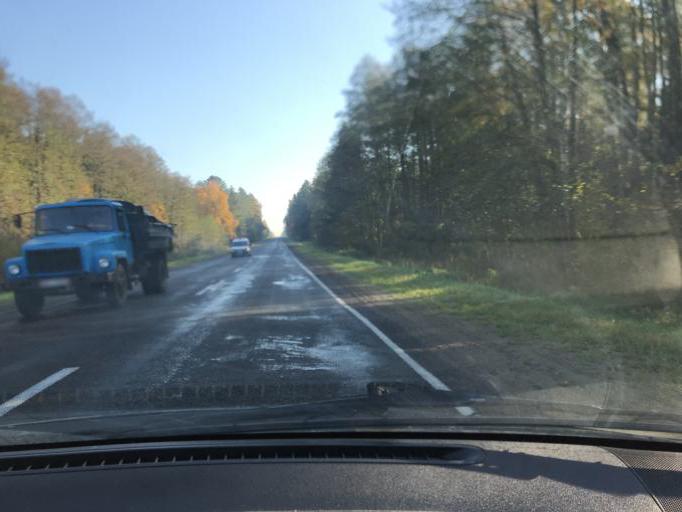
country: BY
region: Brest
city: Lyakhavichy
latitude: 52.9542
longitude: 26.2529
